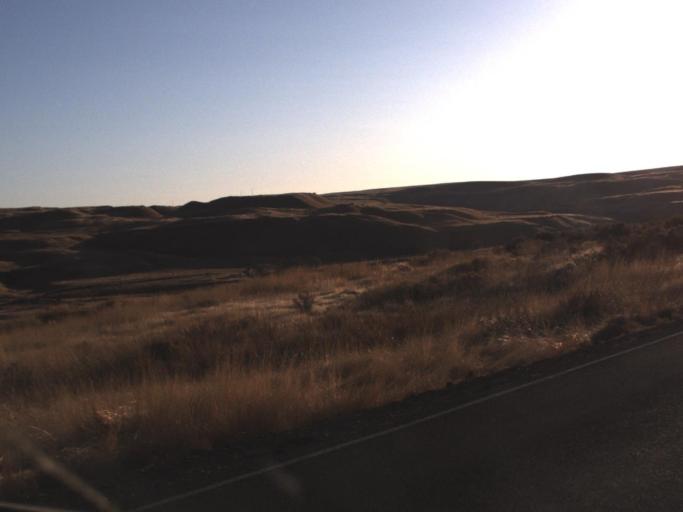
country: US
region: Washington
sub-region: Franklin County
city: Connell
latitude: 46.6479
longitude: -118.5339
